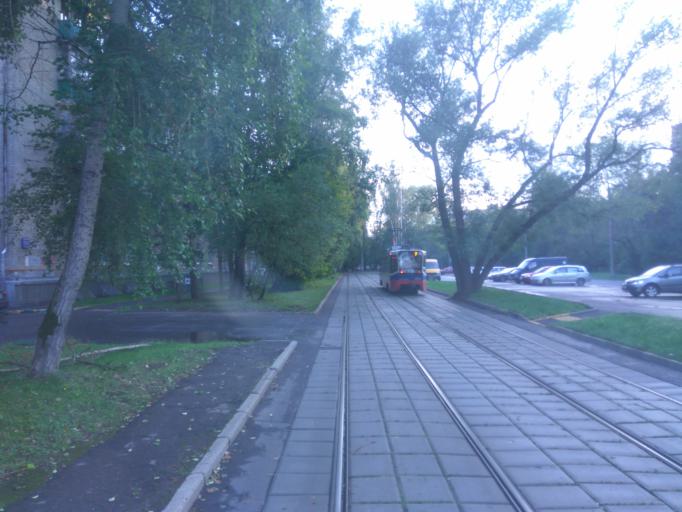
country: RU
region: Moskovskaya
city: Bogorodskoye
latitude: 55.8179
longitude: 37.7207
